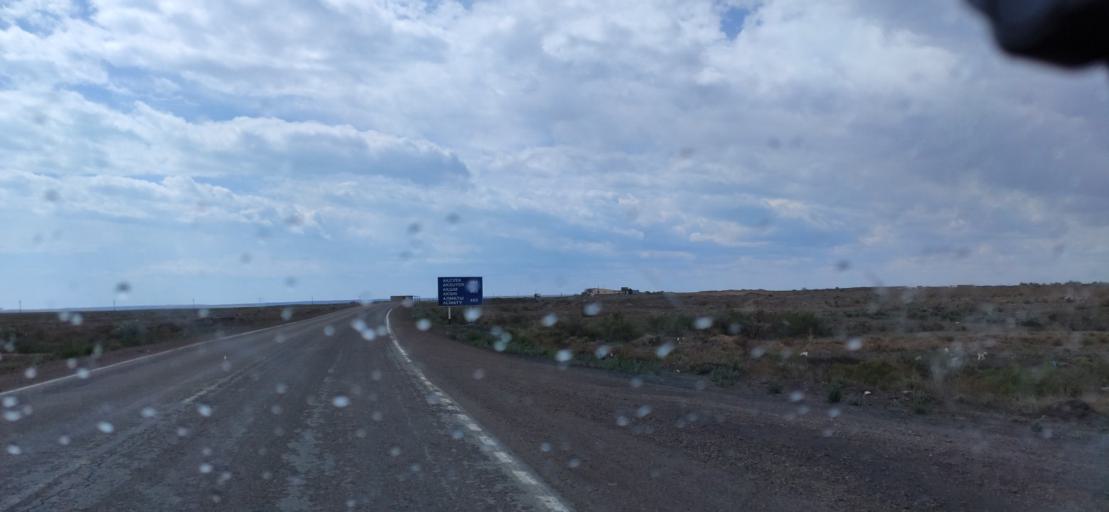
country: KZ
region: Qaraghandy
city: Saryshaghan
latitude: 46.0179
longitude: 73.5917
